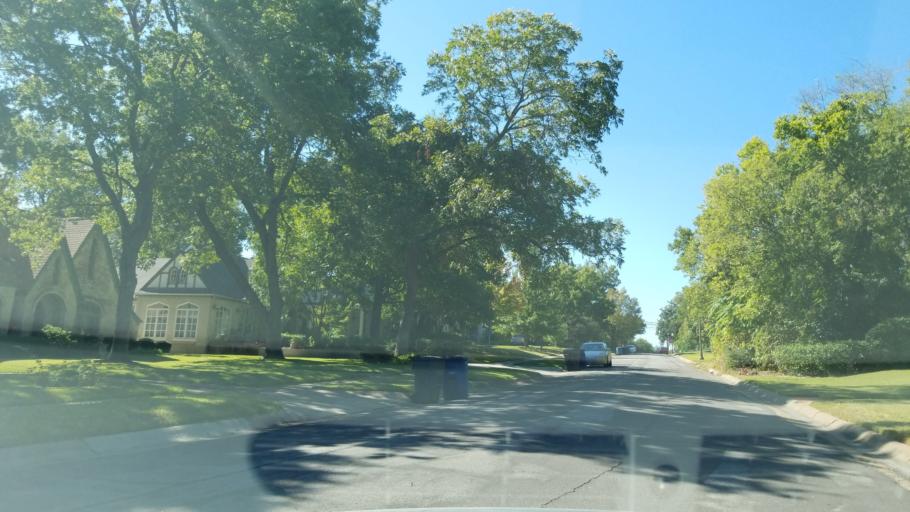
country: US
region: Texas
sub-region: Dallas County
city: Highland Park
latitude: 32.8105
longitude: -96.7503
